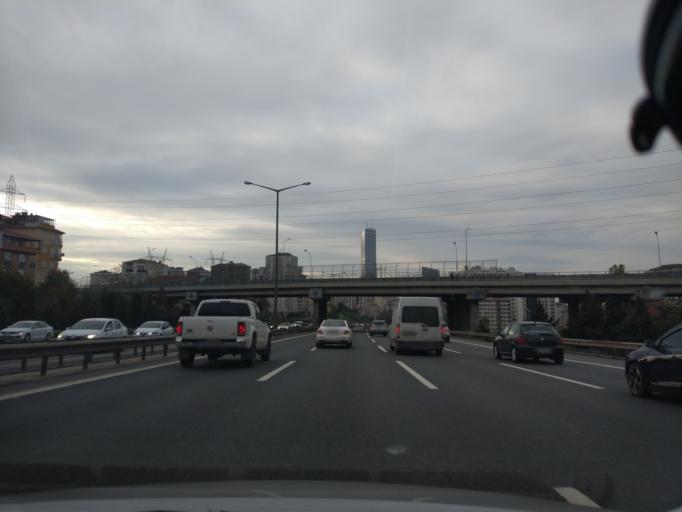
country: TR
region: Istanbul
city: Umraniye
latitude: 41.0111
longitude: 29.1218
